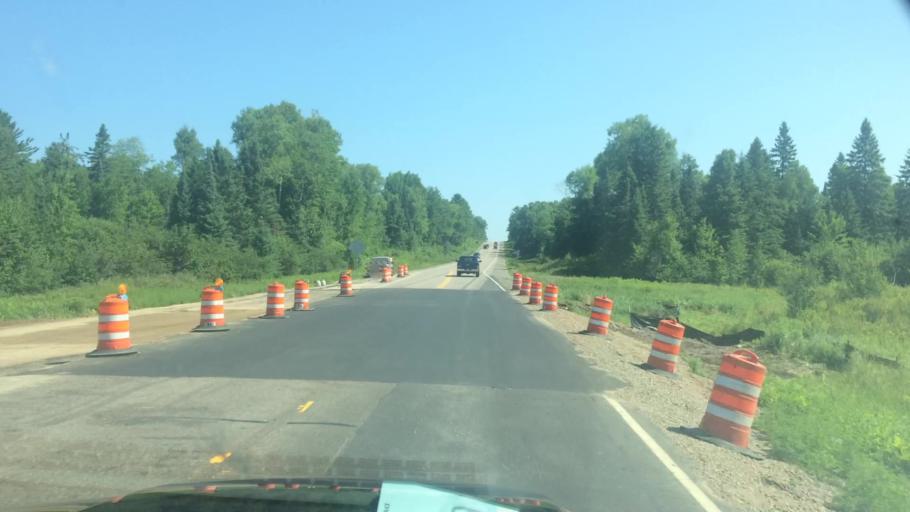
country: US
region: Wisconsin
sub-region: Lincoln County
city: Tomahawk
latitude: 45.5473
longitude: -89.6620
